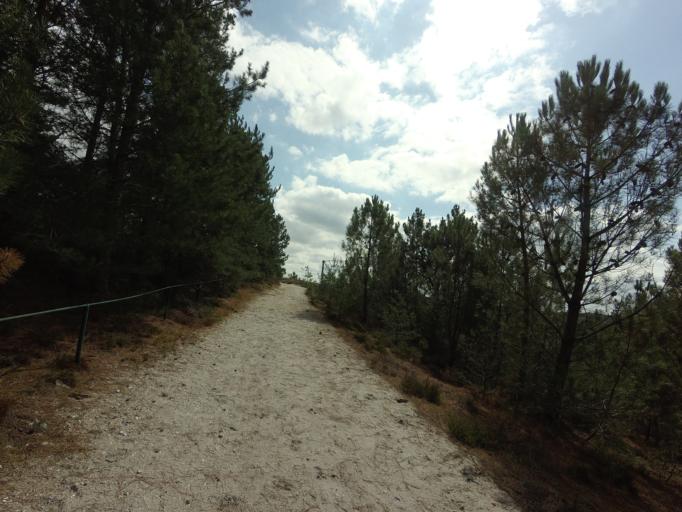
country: NL
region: Limburg
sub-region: Gemeente Brunssum
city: Brunssum
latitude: 50.9272
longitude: 6.0049
